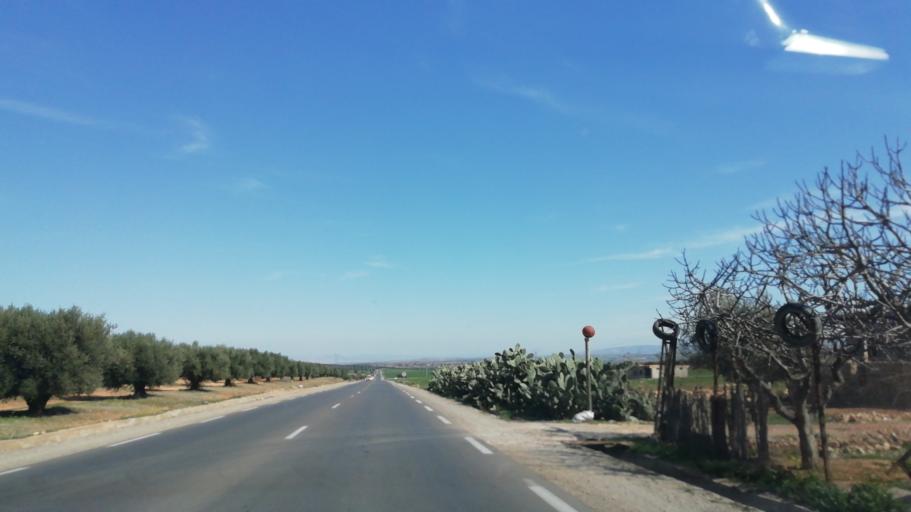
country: DZ
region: Mascara
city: Mascara
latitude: 35.4172
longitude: 0.4059
